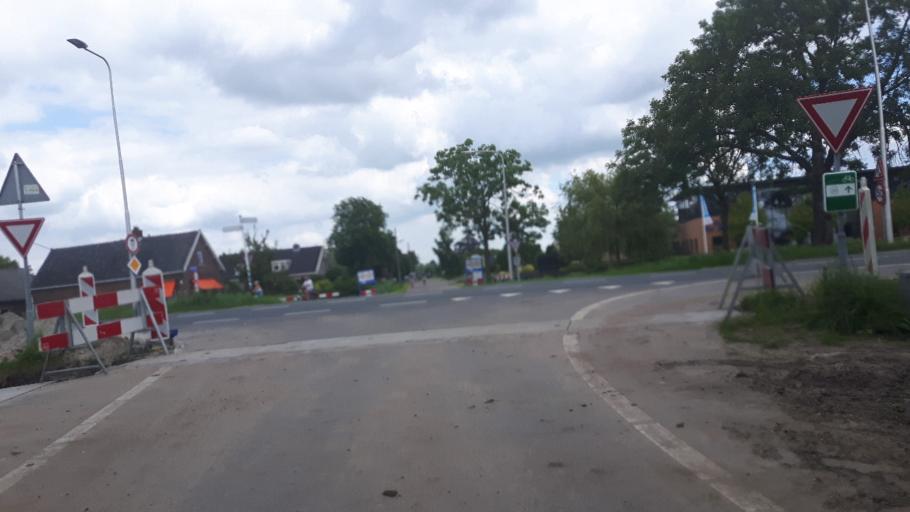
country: NL
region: South Holland
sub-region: Molenwaard
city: Liesveld
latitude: 51.9426
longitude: 4.7796
